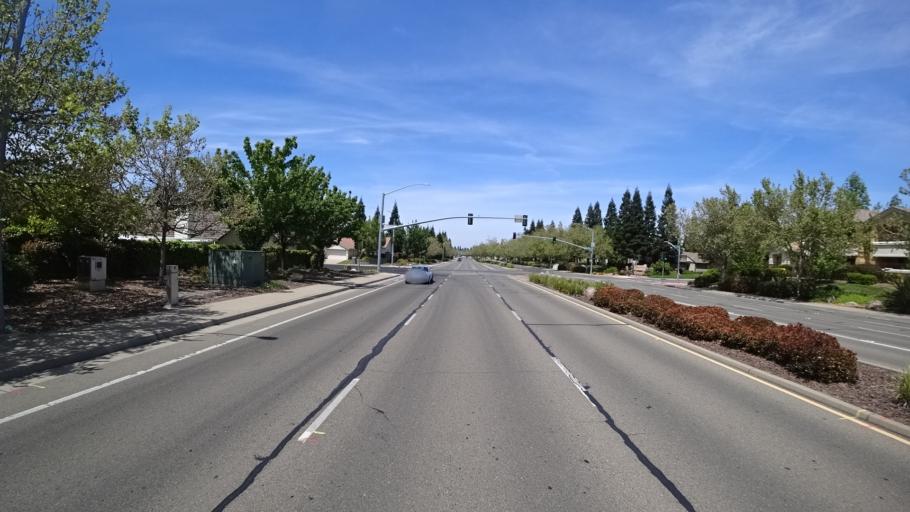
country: US
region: California
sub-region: Placer County
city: Rocklin
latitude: 38.8007
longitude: -121.2697
